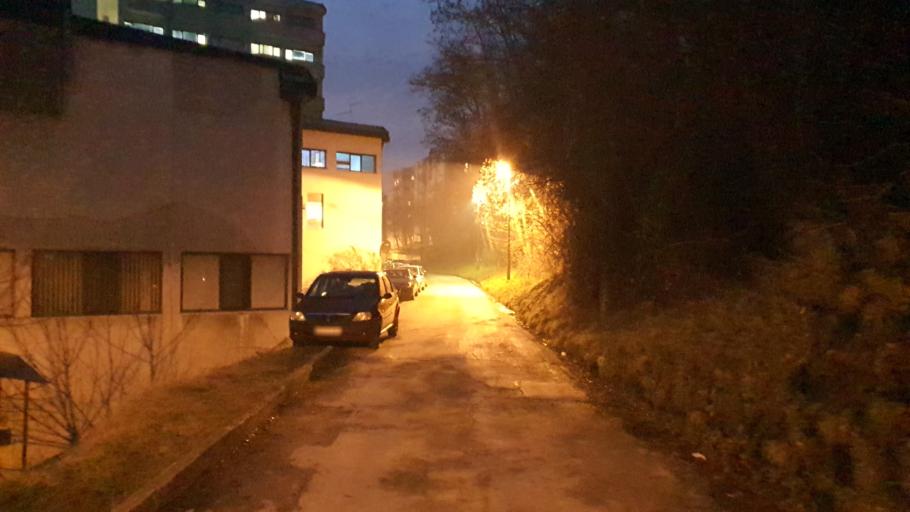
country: RS
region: Central Serbia
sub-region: Zlatiborski Okrug
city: Uzice
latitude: 43.8516
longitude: 19.8606
